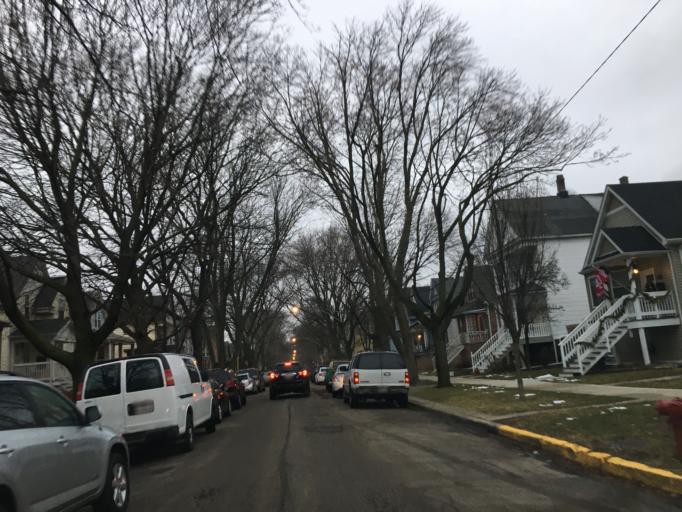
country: US
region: Illinois
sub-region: Cook County
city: Lincolnwood
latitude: 41.9640
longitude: -87.7157
